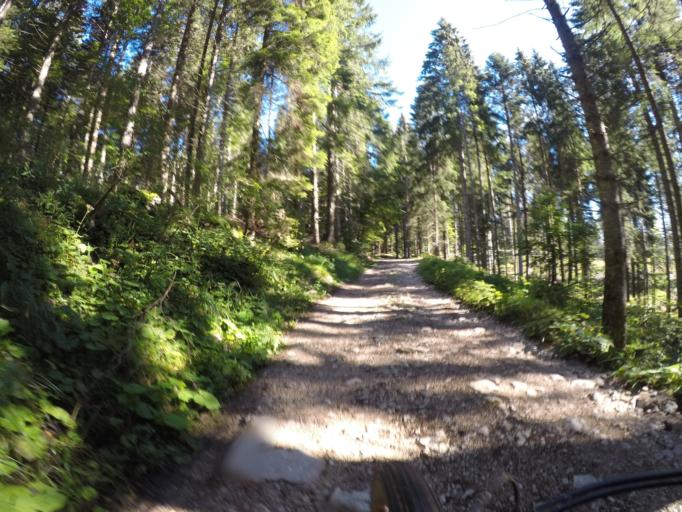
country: IT
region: Veneto
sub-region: Provincia di Vicenza
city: Canove di Roana
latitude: 45.9000
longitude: 11.4827
